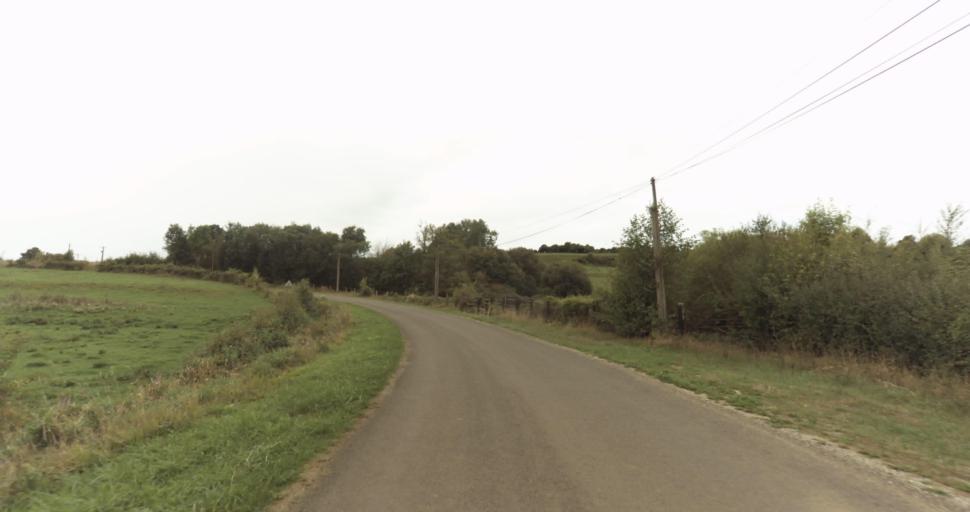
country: FR
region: Lower Normandy
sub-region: Departement de l'Orne
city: Gace
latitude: 48.7639
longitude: 0.3294
